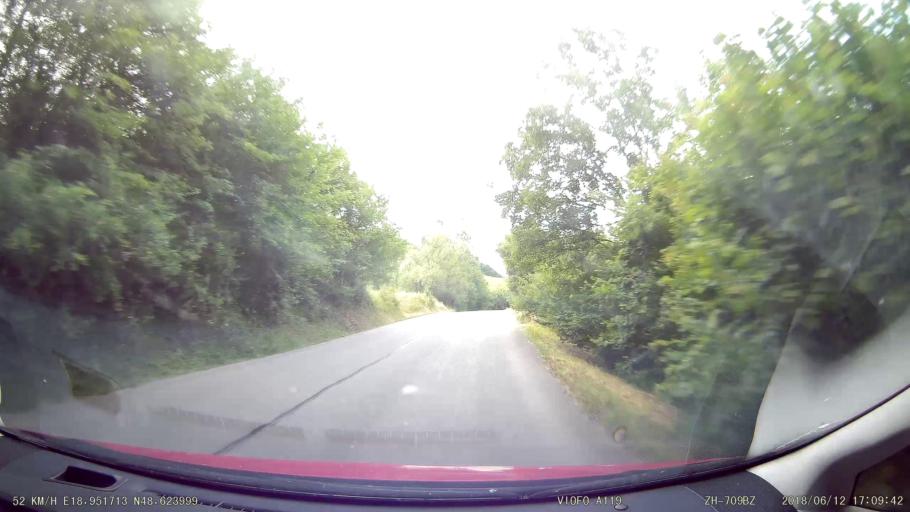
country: SK
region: Banskobystricky
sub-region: Okres Ziar nad Hronom
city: Kremnica
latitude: 48.6242
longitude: 18.9516
